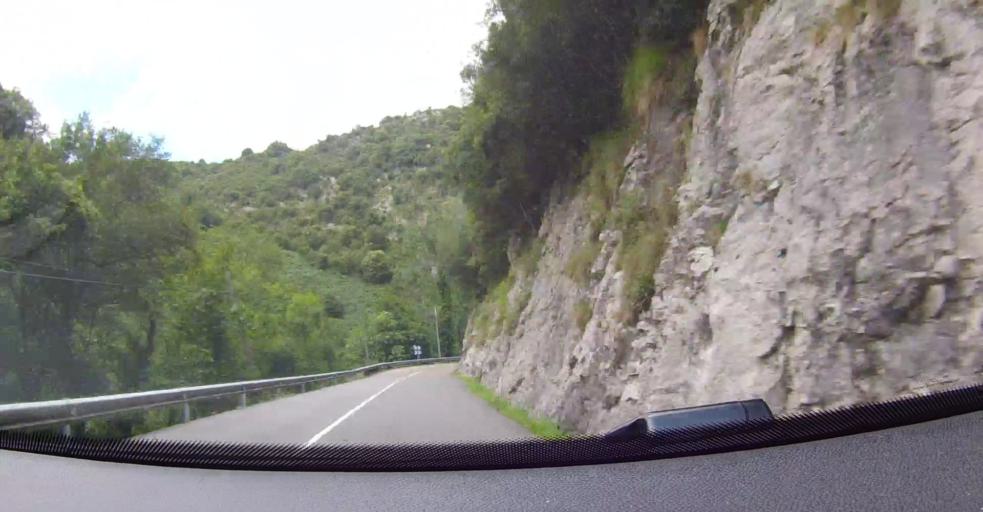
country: ES
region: Cantabria
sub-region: Provincia de Cantabria
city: Tresviso
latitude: 43.3097
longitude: -4.6085
